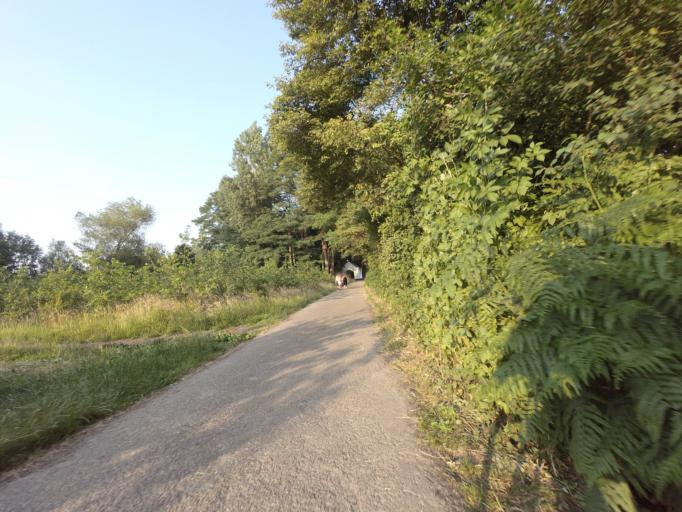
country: BE
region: Flanders
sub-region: Provincie Antwerpen
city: Lint
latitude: 51.1218
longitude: 4.4787
